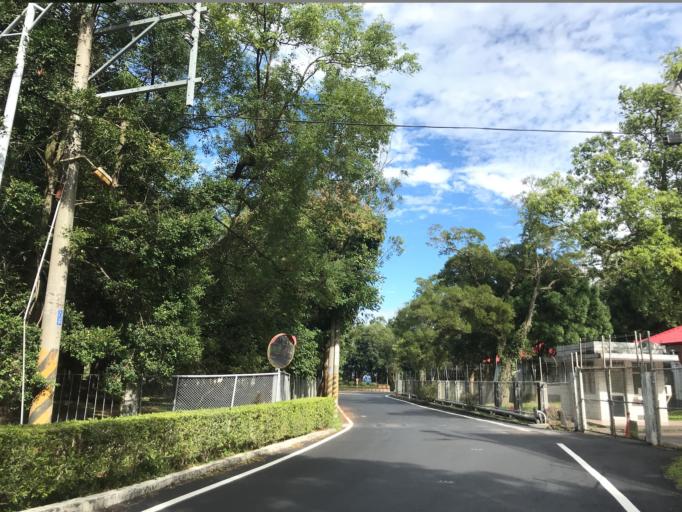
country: TW
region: Taiwan
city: Daxi
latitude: 24.8379
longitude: 121.2412
